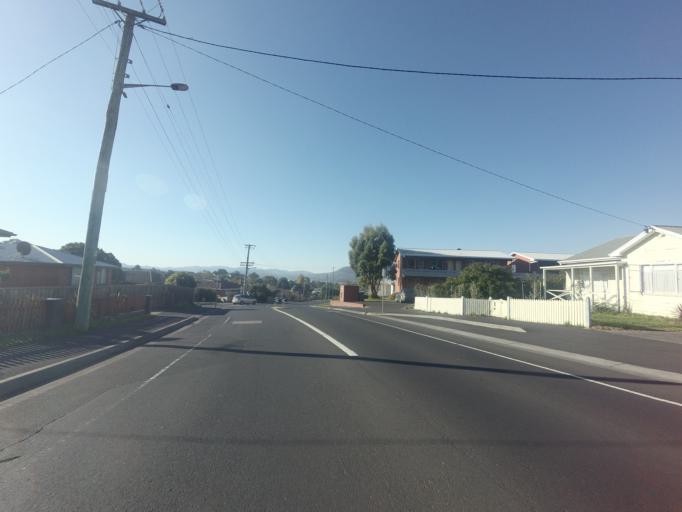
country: AU
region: Tasmania
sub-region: Glenorchy
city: Glenorchy
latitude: -42.8453
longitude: 147.2655
